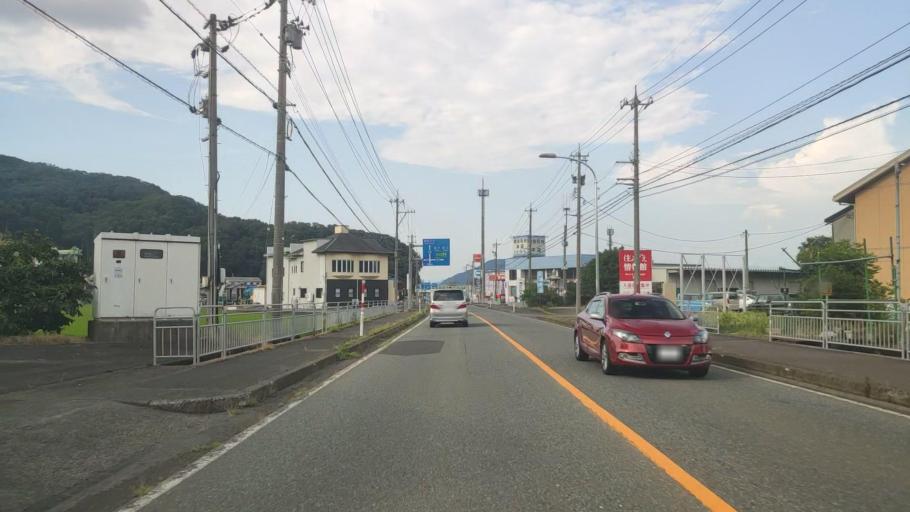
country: JP
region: Fukui
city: Takefu
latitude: 35.8699
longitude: 136.1544
